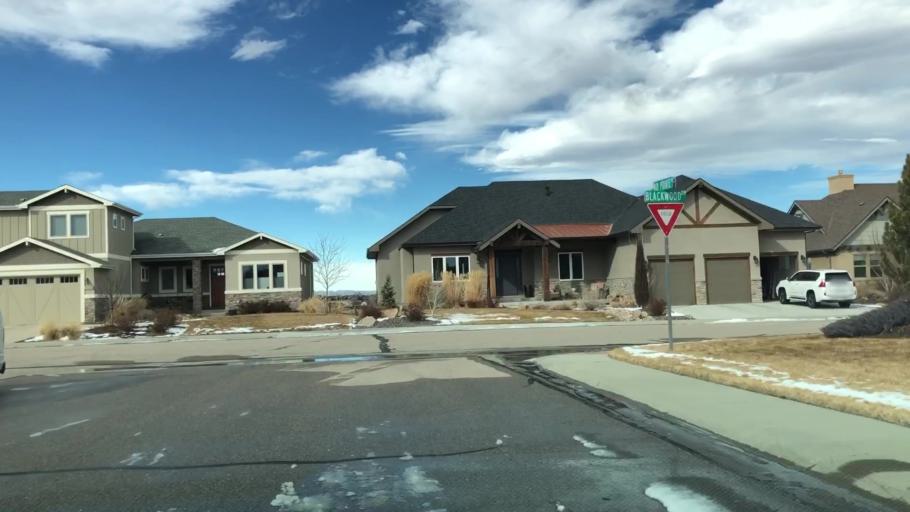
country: US
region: Colorado
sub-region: Weld County
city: Windsor
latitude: 40.4547
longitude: -104.9560
